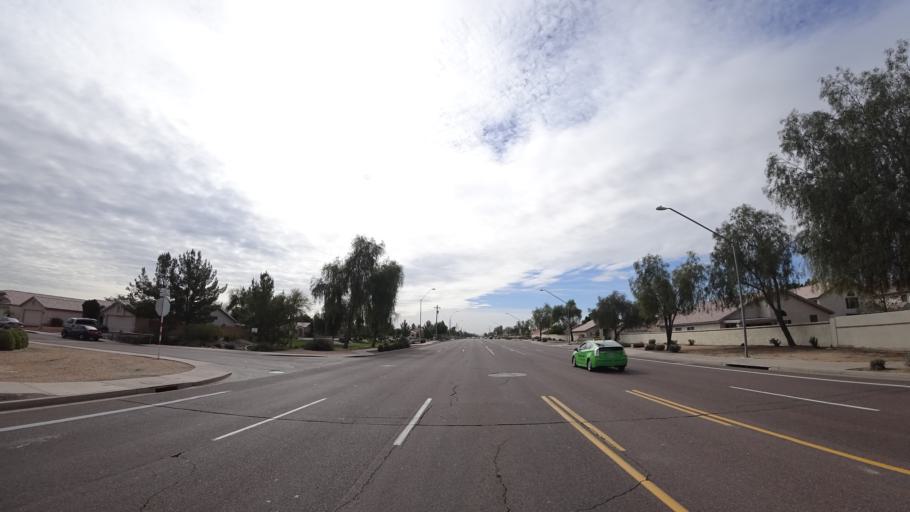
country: US
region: Arizona
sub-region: Maricopa County
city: Peoria
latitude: 33.6599
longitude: -112.1691
